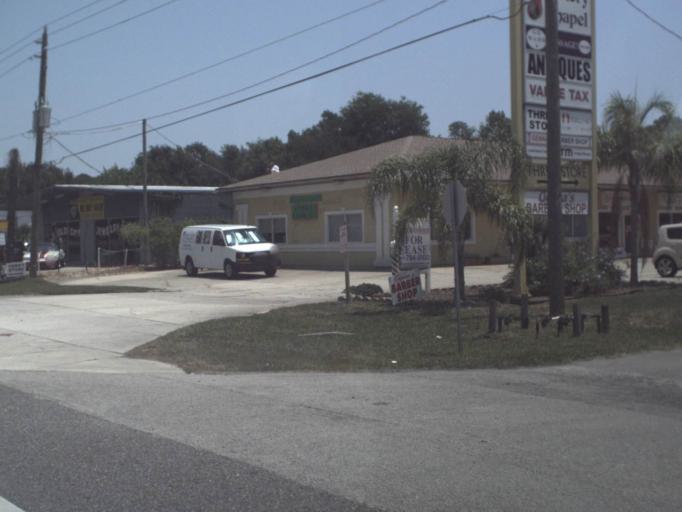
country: US
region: Florida
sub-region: Saint Johns County
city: Saint Augustine South
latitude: 29.8485
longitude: -81.3225
